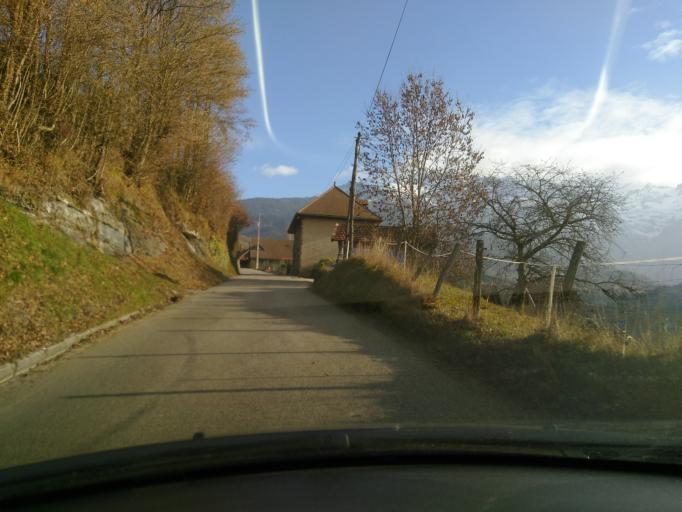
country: FR
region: Rhone-Alpes
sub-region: Departement de l'Isere
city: Villard-Bonnot
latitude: 45.2370
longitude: 5.9195
